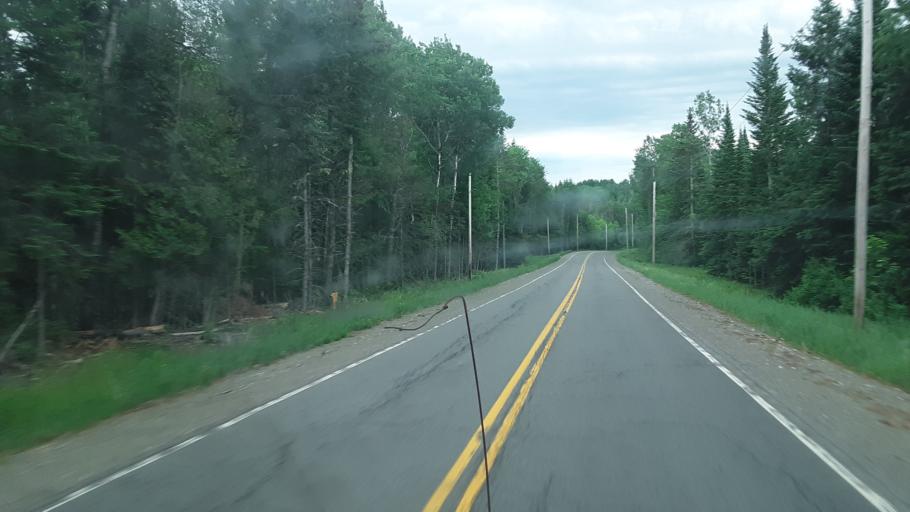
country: US
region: Maine
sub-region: Penobscot County
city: Patten
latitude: 45.7923
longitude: -68.3219
